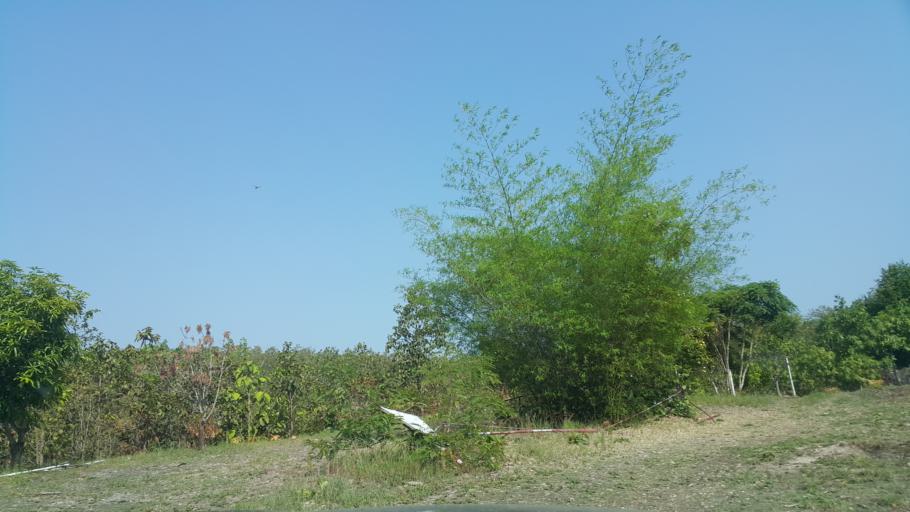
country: TH
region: Chiang Mai
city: Hang Dong
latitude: 18.6960
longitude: 98.8799
